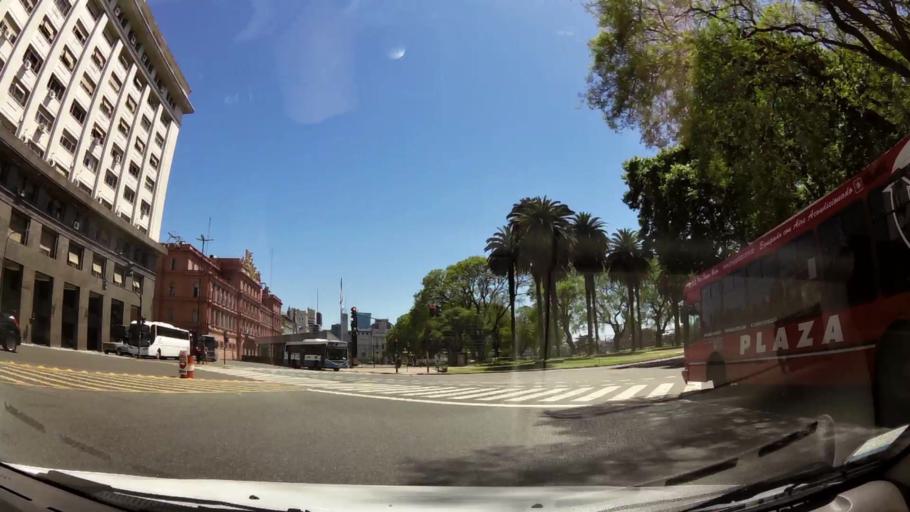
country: AR
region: Buenos Aires F.D.
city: Buenos Aires
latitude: -34.6096
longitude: -58.3694
